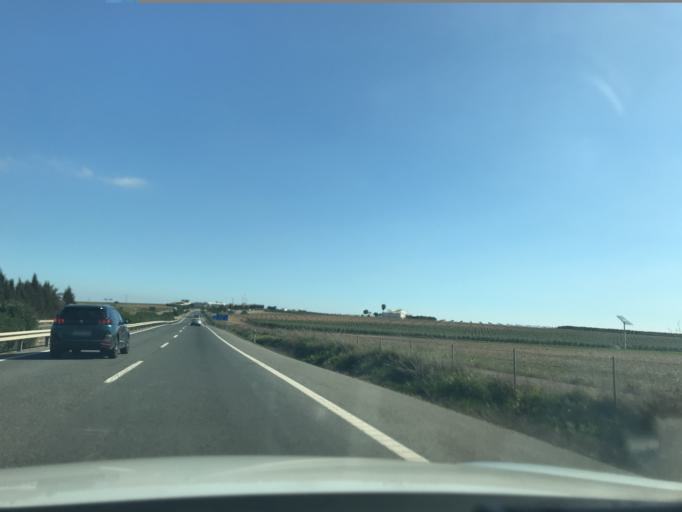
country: ES
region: Andalusia
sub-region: Provincia de Sevilla
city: Ecija
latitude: 37.5798
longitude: -4.9943
